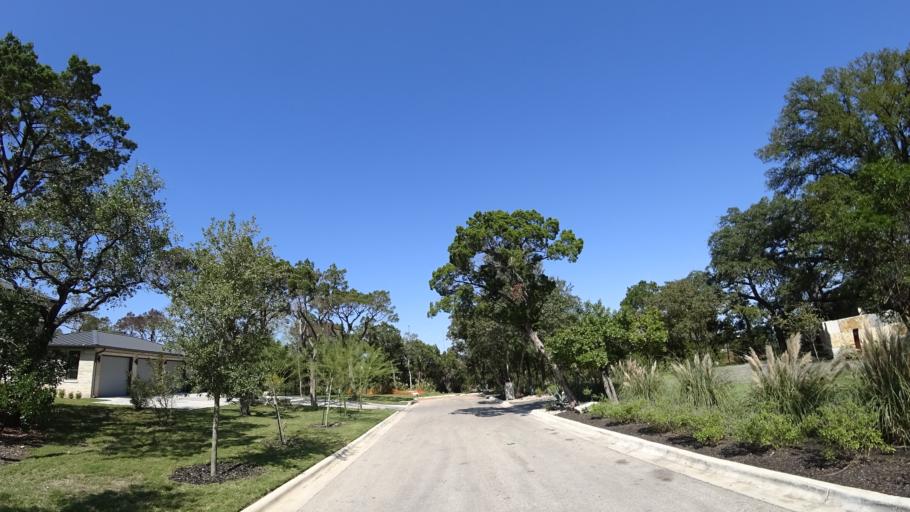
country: US
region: Texas
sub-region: Travis County
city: West Lake Hills
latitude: 30.2976
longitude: -97.8061
